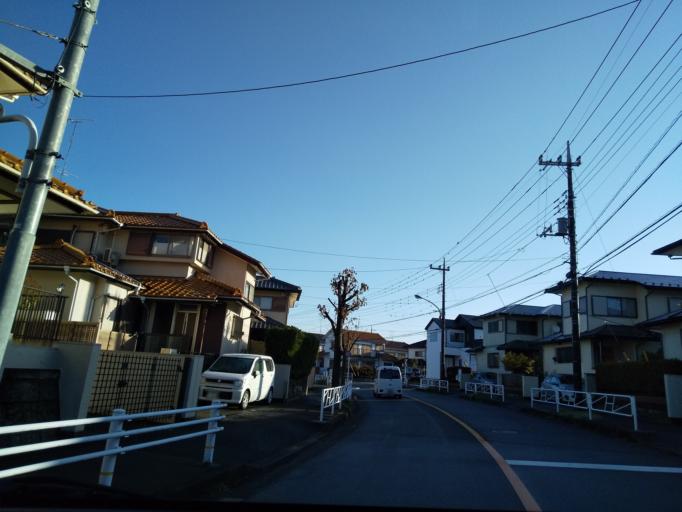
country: JP
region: Tokyo
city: Hachioji
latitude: 35.6250
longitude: 139.3561
